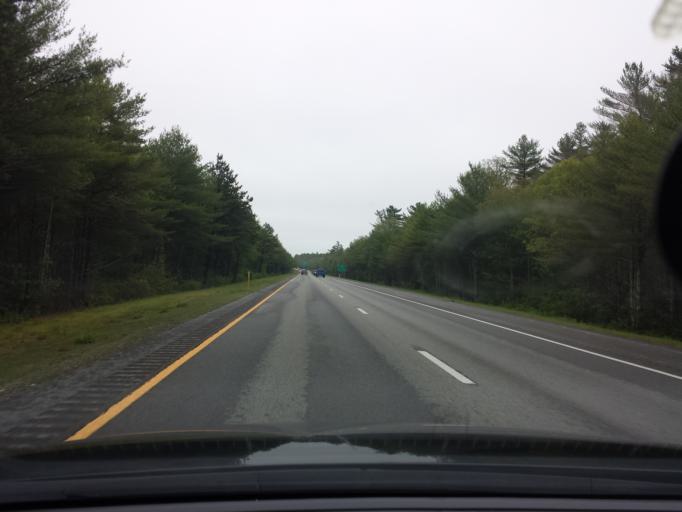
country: US
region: Massachusetts
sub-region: Plymouth County
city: Marion Center
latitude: 41.7119
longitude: -70.7900
